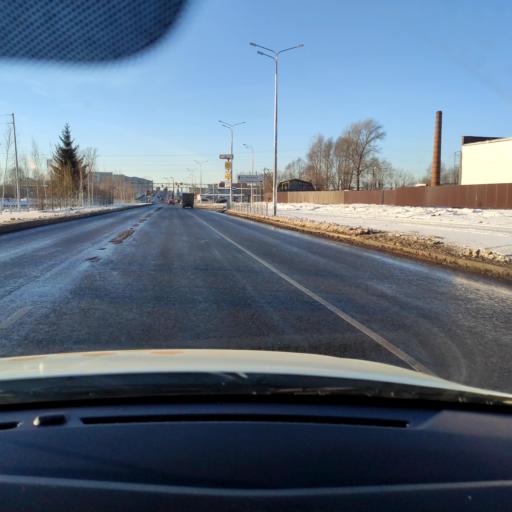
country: RU
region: Tatarstan
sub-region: Gorod Kazan'
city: Kazan
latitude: 55.7307
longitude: 49.1373
